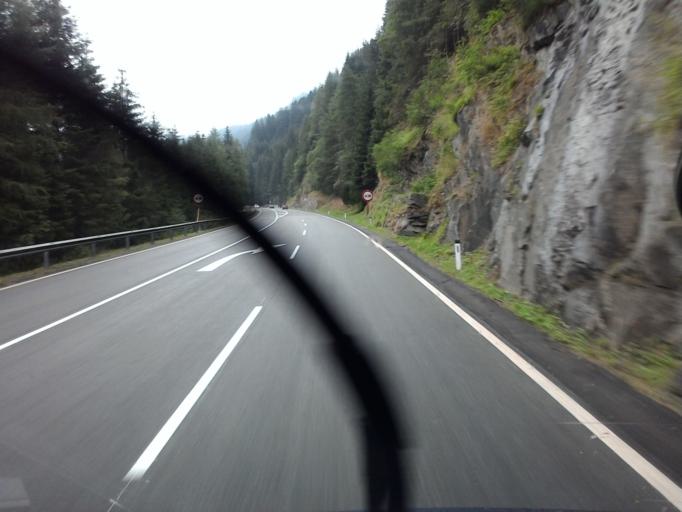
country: AT
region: Tyrol
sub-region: Politischer Bezirk Lienz
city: Matrei in Osttirol
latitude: 47.0540
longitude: 12.5222
